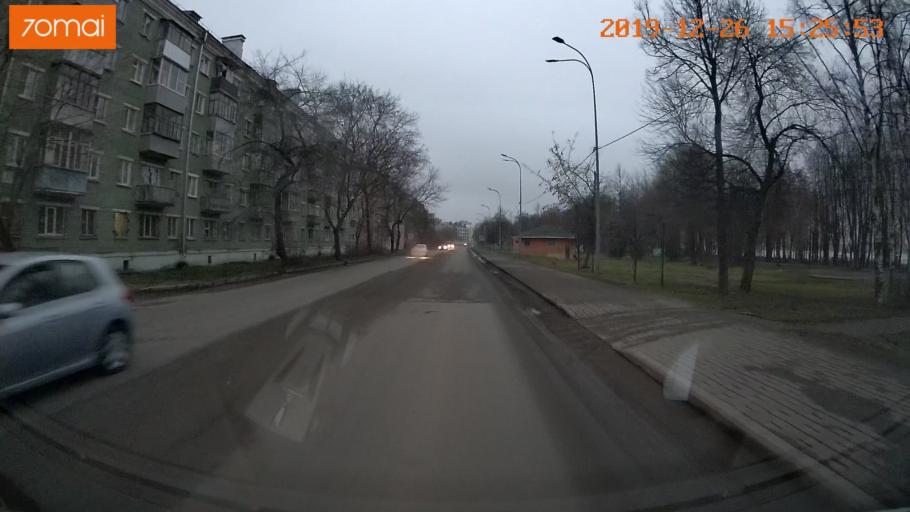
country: RU
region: Jaroslavl
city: Rybinsk
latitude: 58.0550
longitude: 38.8341
